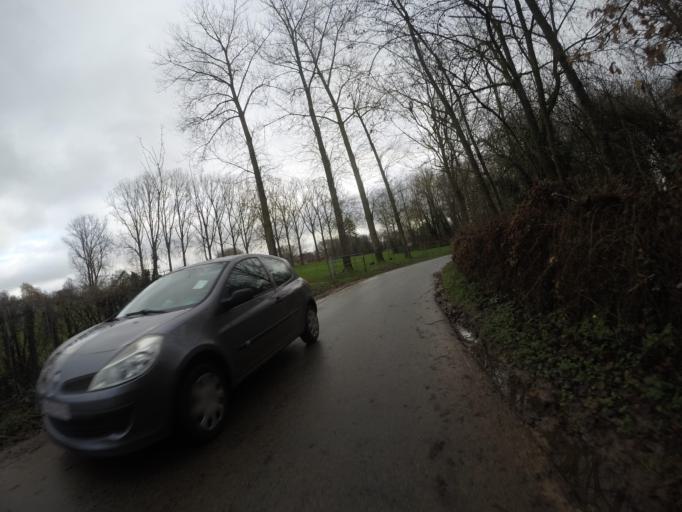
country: BE
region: Flanders
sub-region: Provincie Vlaams-Brabant
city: Gooik
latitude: 50.8154
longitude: 4.1140
